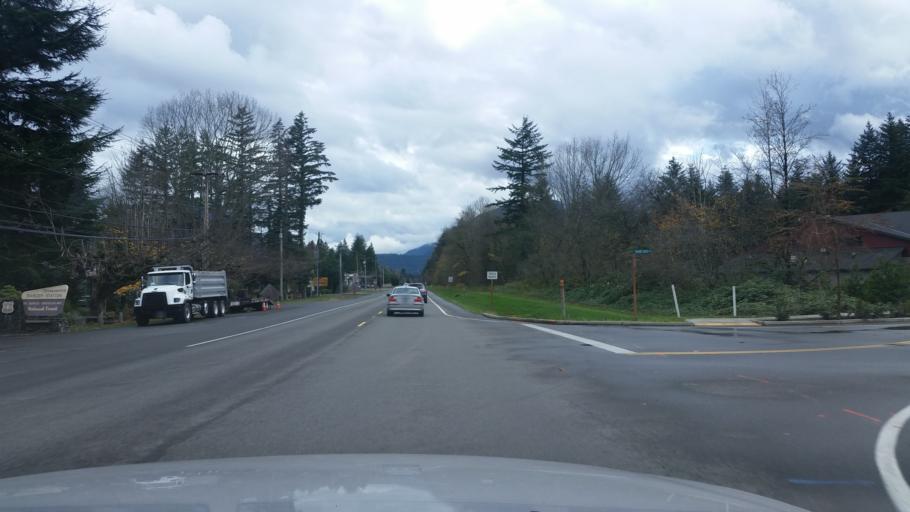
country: US
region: Washington
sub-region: King County
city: North Bend
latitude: 47.4892
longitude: -121.7747
